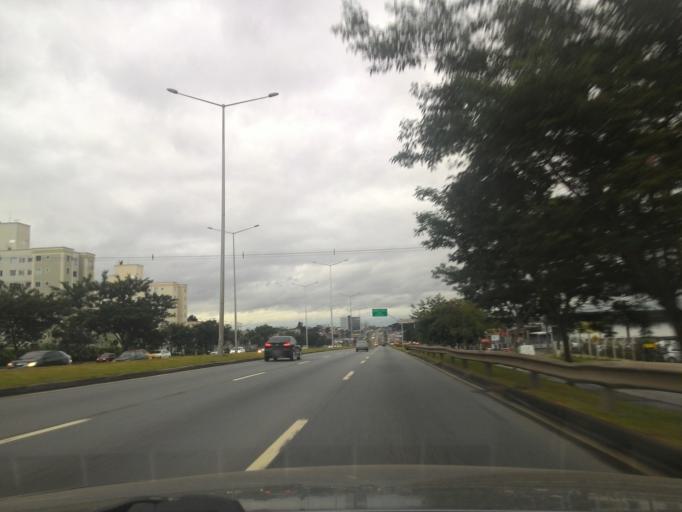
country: BR
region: Parana
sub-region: Sao Jose Dos Pinhais
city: Sao Jose dos Pinhais
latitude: -25.5109
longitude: -49.2876
